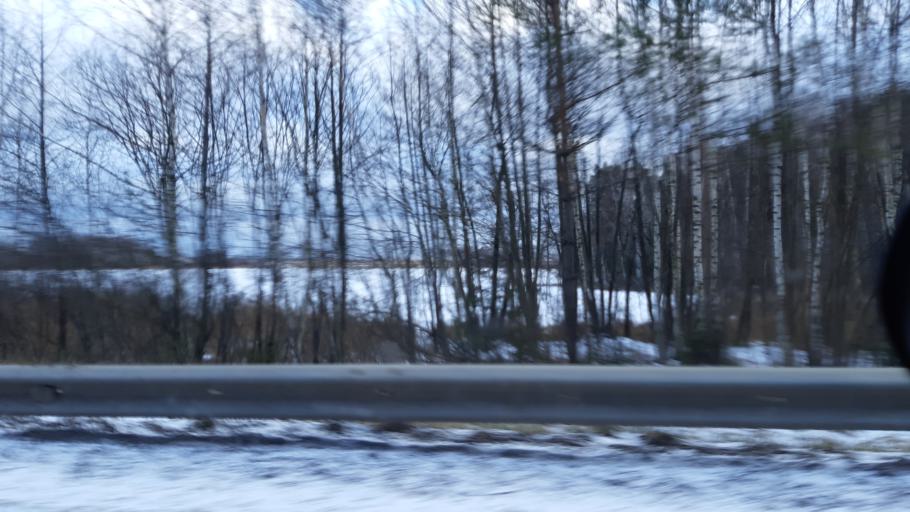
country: RU
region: Moskovskaya
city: Noginsk-9
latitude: 55.9818
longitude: 38.5441
